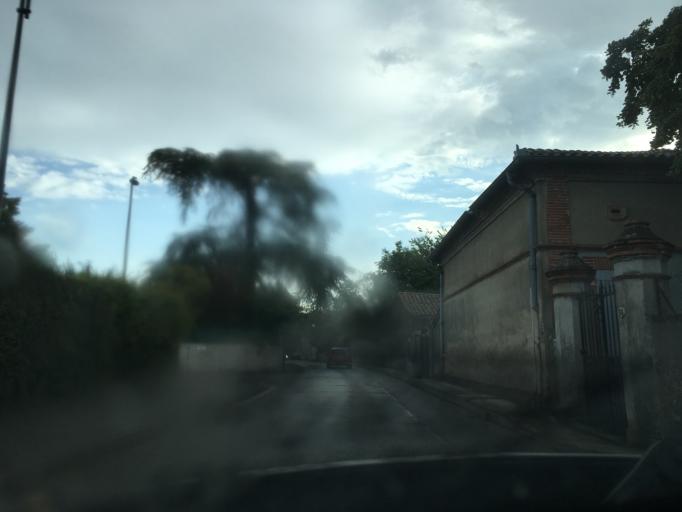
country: FR
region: Midi-Pyrenees
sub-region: Departement de la Haute-Garonne
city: Portet-sur-Garonne
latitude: 43.5588
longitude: 1.3821
